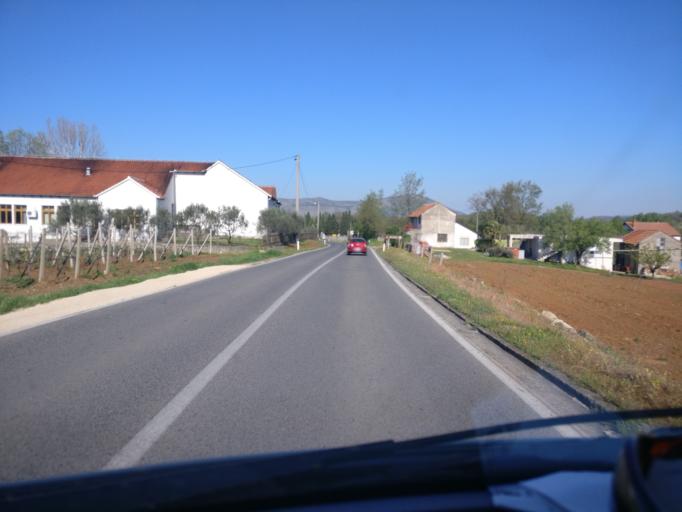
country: BA
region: Federation of Bosnia and Herzegovina
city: Tasovcici
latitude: 43.1362
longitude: 17.7864
